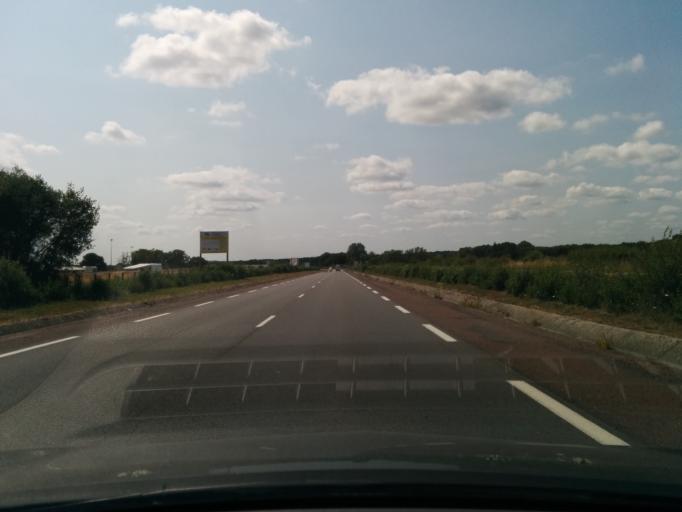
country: FR
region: Centre
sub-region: Departement du Cher
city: Vierzon
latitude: 47.2445
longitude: 2.0811
